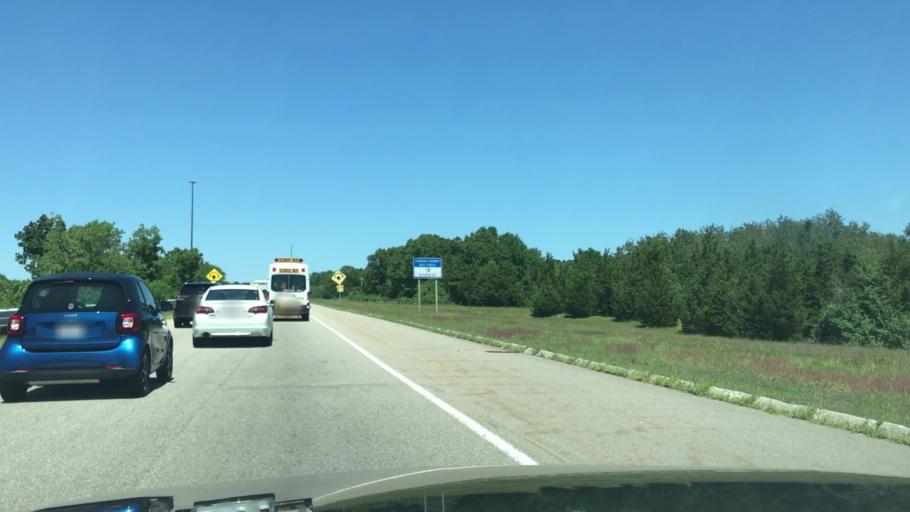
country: US
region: Massachusetts
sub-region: Norfolk County
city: Dedham
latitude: 42.2050
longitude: -71.1414
